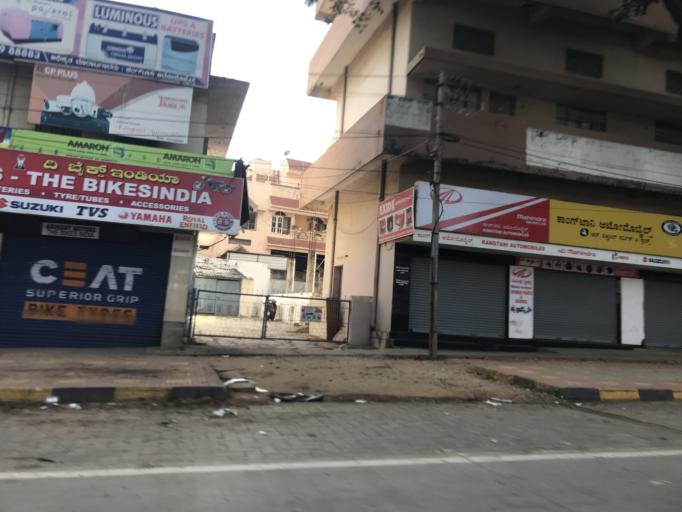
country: IN
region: Karnataka
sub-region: Mysore
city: Mysore
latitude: 12.3019
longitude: 76.6483
